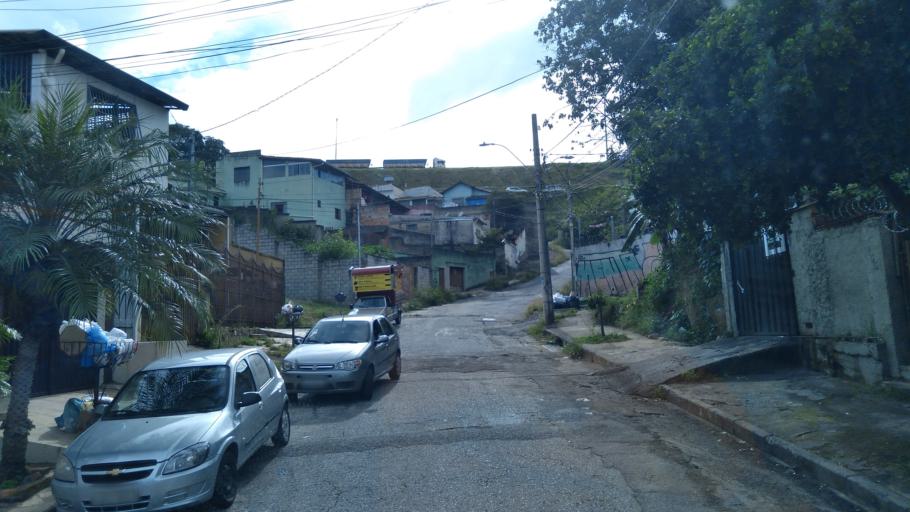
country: BR
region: Minas Gerais
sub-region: Belo Horizonte
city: Belo Horizonte
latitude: -19.9133
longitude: -43.9952
